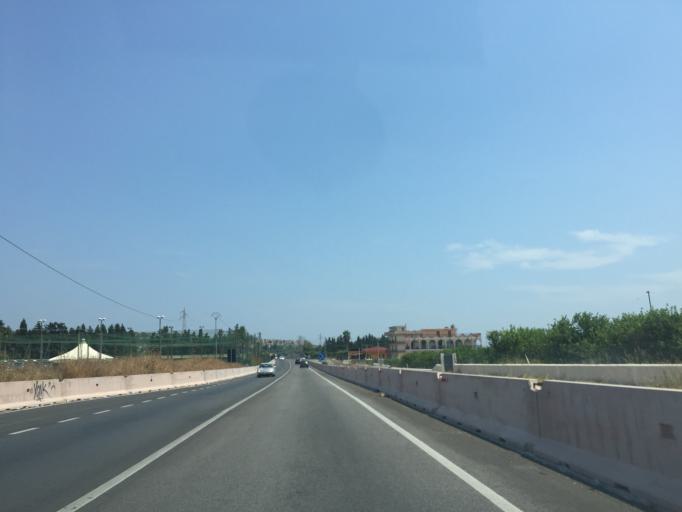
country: IT
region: Sicily
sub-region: Provincia di Siracusa
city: Belvedere
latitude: 37.0733
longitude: 15.2404
